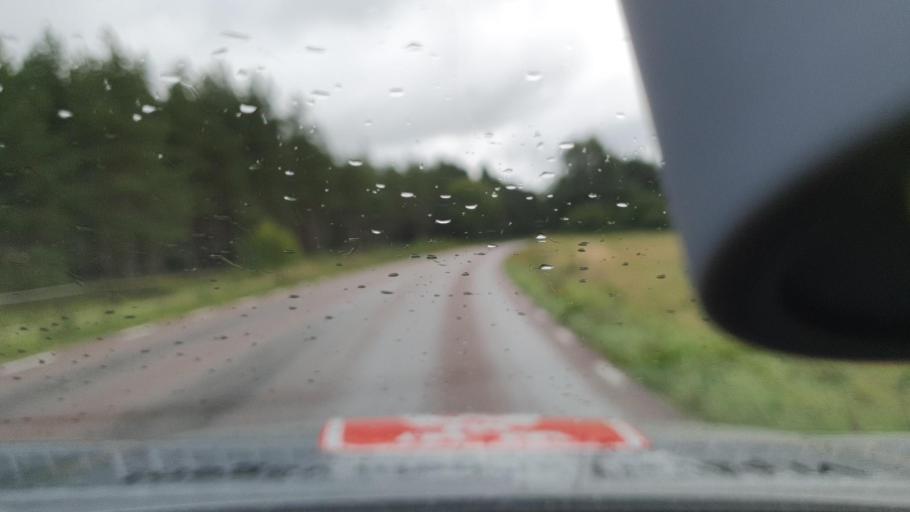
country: SE
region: Gotland
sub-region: Gotland
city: Hemse
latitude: 57.1390
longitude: 18.3482
